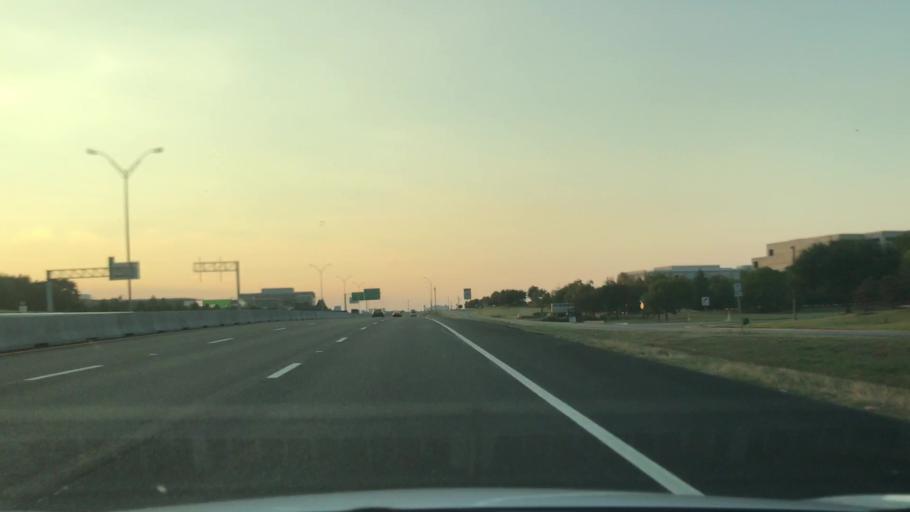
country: US
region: Texas
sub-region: Dallas County
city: Coppell
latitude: 32.8966
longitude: -96.9736
